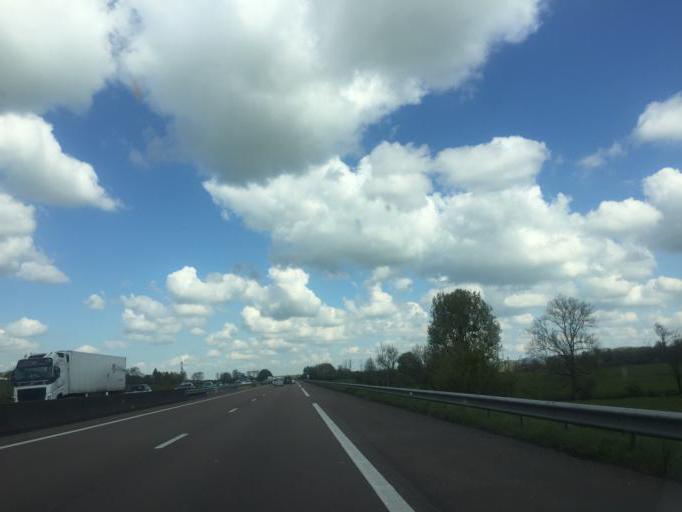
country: FR
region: Bourgogne
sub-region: Departement de la Cote-d'Or
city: Pouilly-en-Auxois
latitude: 47.3185
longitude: 4.4937
